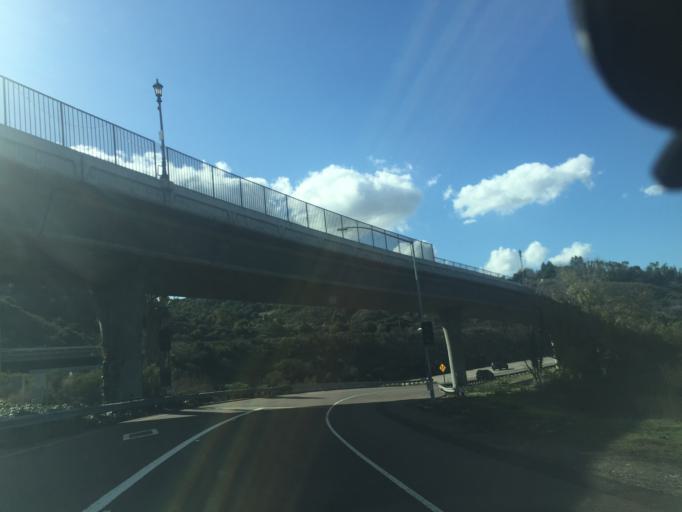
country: US
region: California
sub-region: San Diego County
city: La Mesa
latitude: 32.7819
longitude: -117.0876
